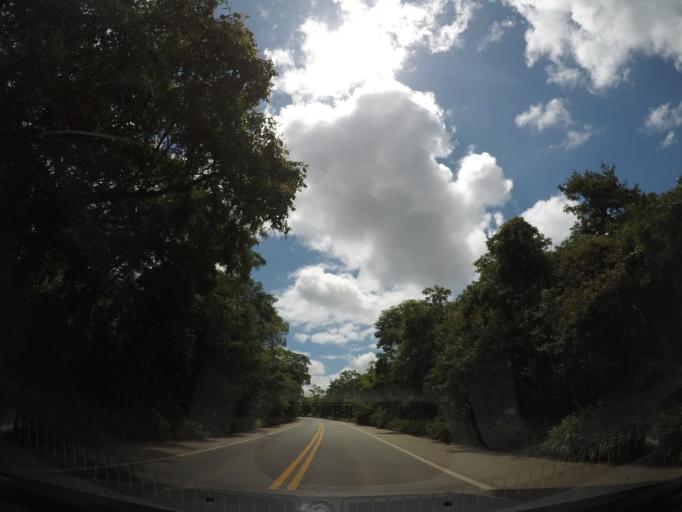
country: BR
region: Bahia
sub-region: Iraquara
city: Iraquara
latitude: -12.4815
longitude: -41.3553
